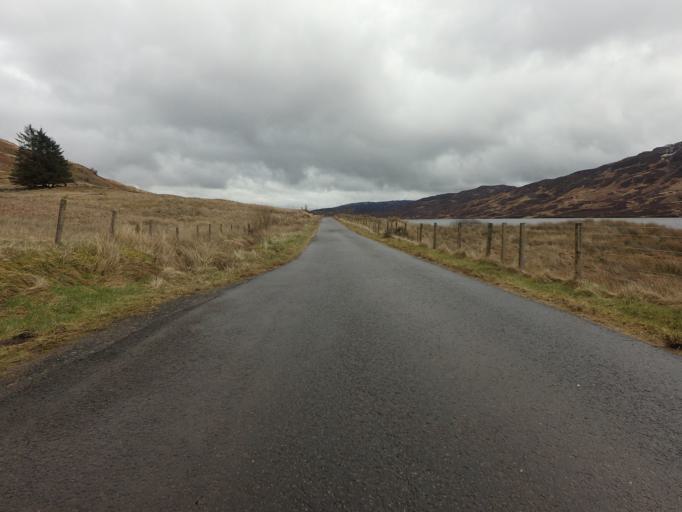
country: GB
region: Scotland
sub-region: West Dunbartonshire
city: Balloch
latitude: 56.2496
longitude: -4.6216
